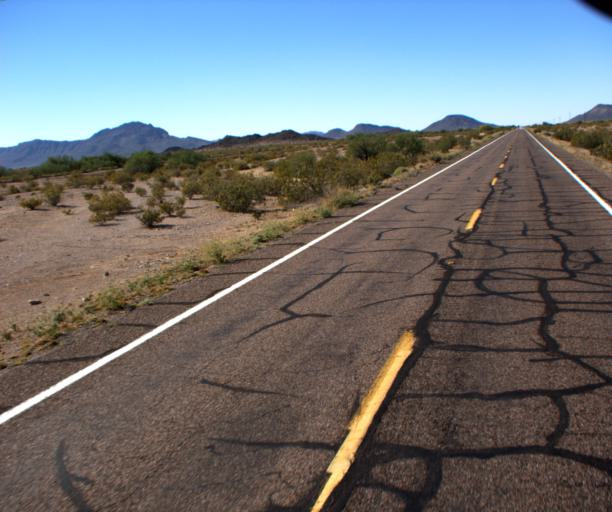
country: US
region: Arizona
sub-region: Maricopa County
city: Gila Bend
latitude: 32.8176
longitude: -112.7898
